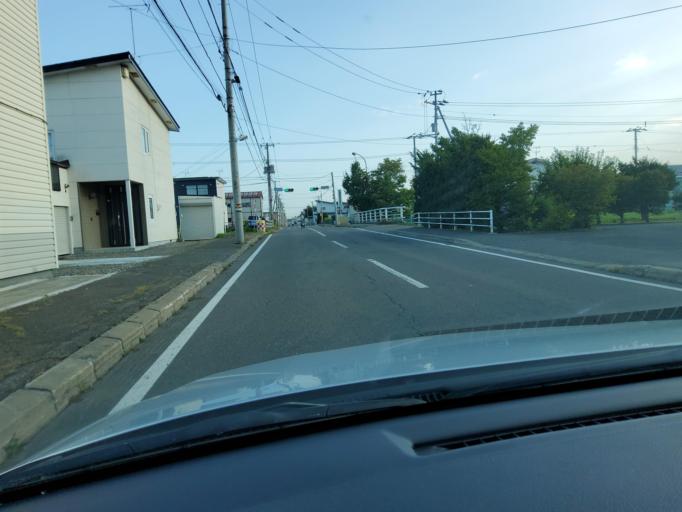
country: JP
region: Hokkaido
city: Obihiro
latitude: 42.9387
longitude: 143.1827
